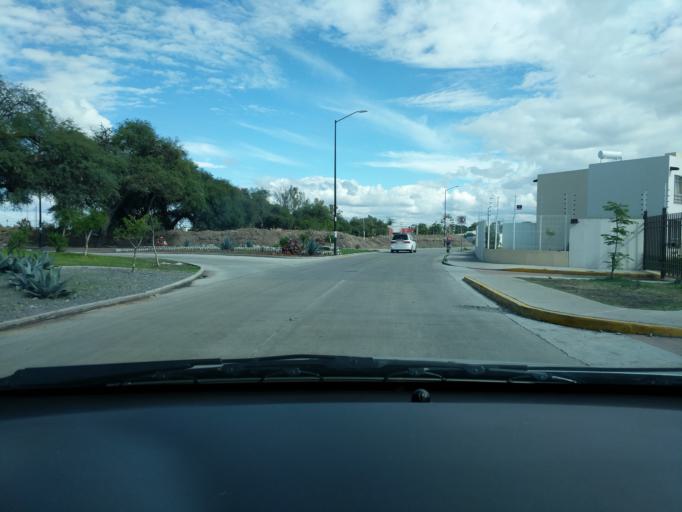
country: MX
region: Queretaro
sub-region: El Marques
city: La Loma
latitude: 20.5841
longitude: -100.2546
